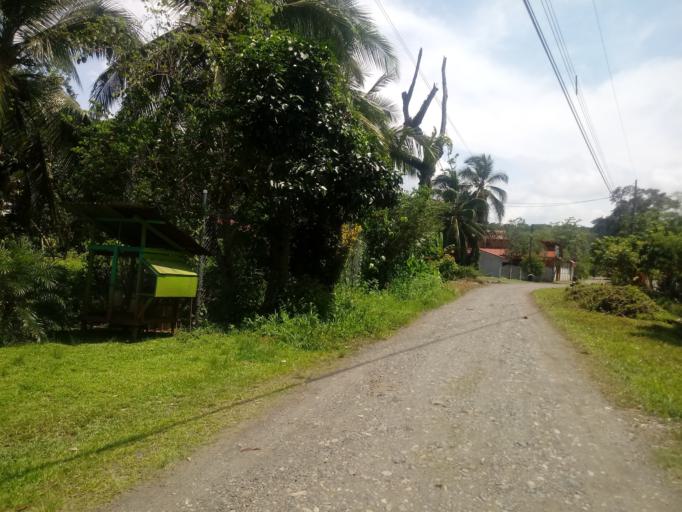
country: CR
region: Limon
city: Sixaola
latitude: 9.6317
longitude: -82.6578
